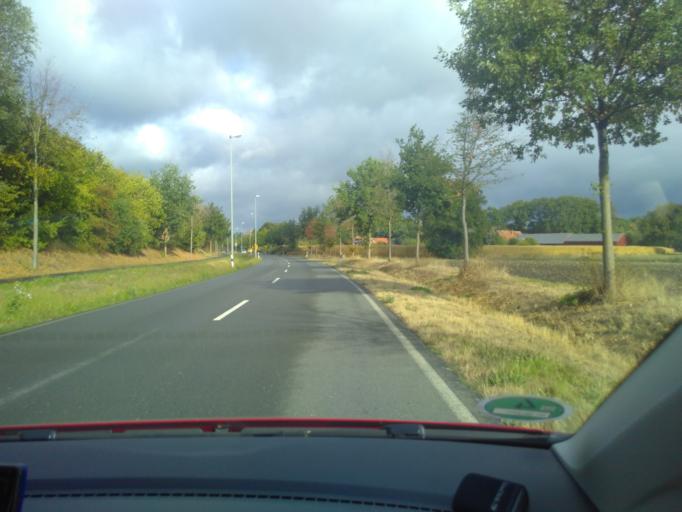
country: DE
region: North Rhine-Westphalia
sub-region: Regierungsbezirk Munster
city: Warendorf
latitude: 51.9603
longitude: 8.0084
